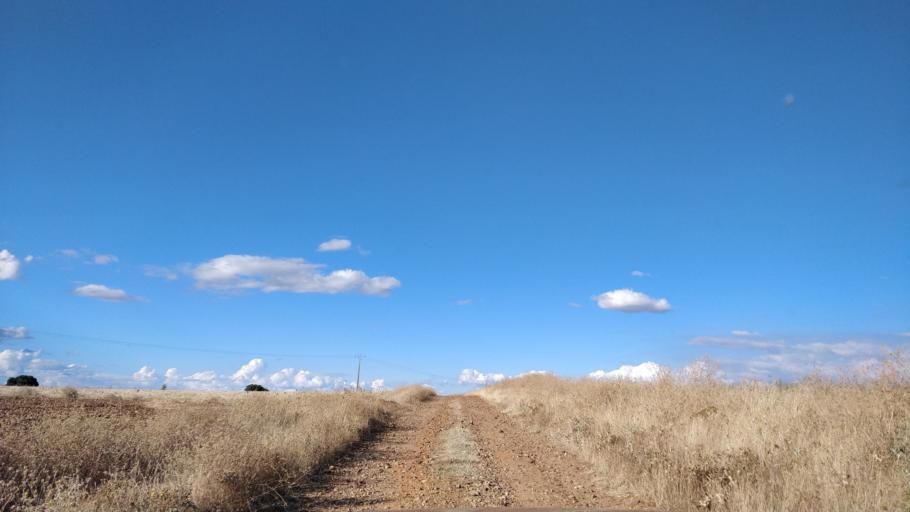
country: ES
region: Castille and Leon
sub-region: Provincia de Leon
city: Santa Cristina de Valmadrigal
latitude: 42.3386
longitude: -5.2741
